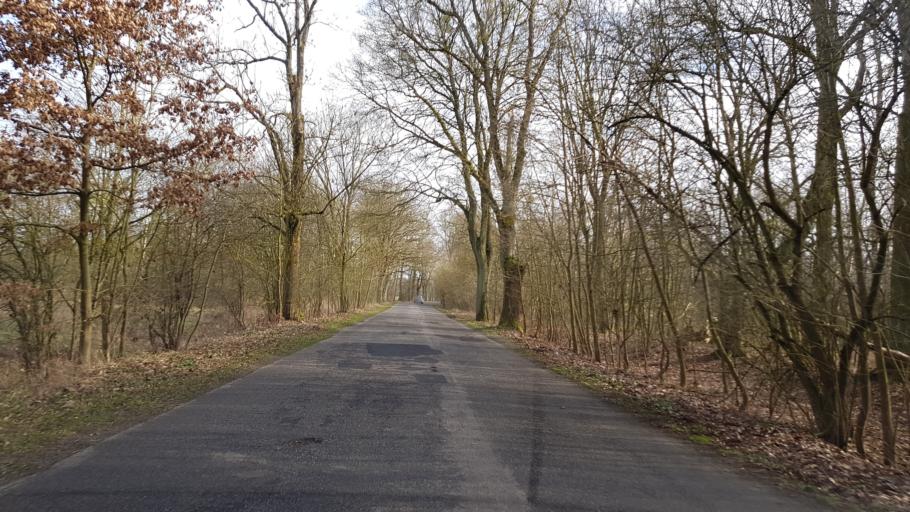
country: PL
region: West Pomeranian Voivodeship
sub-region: Powiat policki
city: Dobra
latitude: 53.5378
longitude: 14.3184
